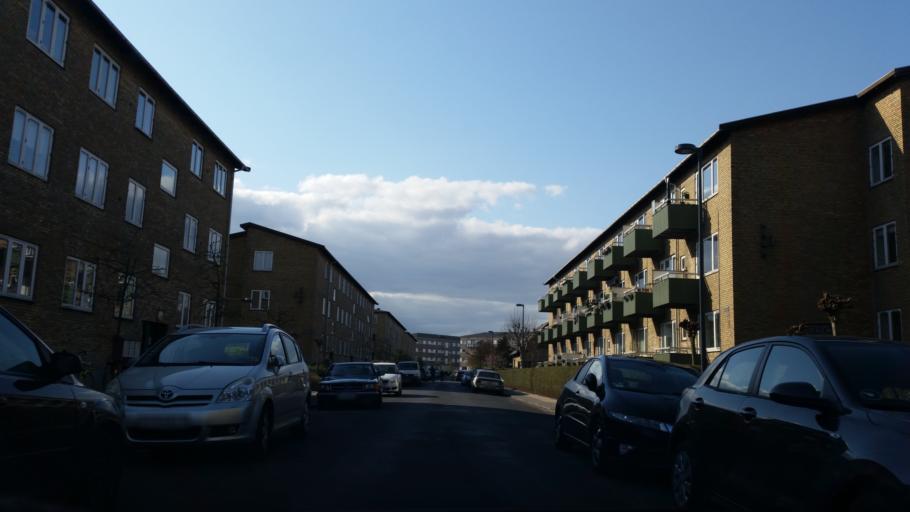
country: DK
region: Capital Region
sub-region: Kobenhavn
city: Christianshavn
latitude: 55.6580
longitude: 12.6236
